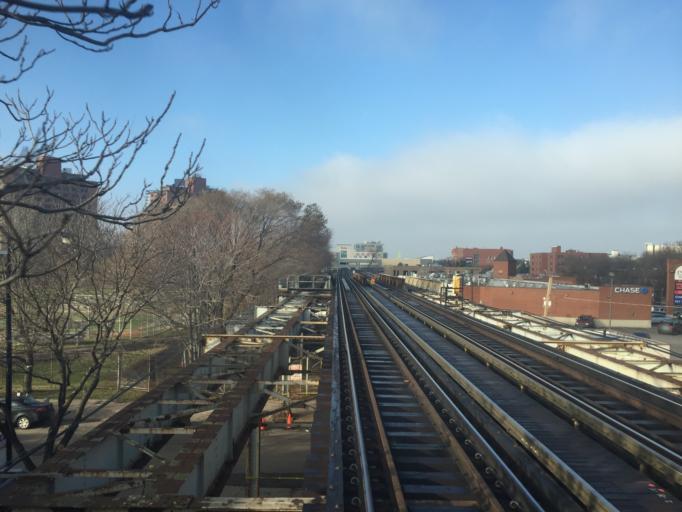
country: US
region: Illinois
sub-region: Cook County
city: Chicago
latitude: 41.9104
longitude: -87.6432
